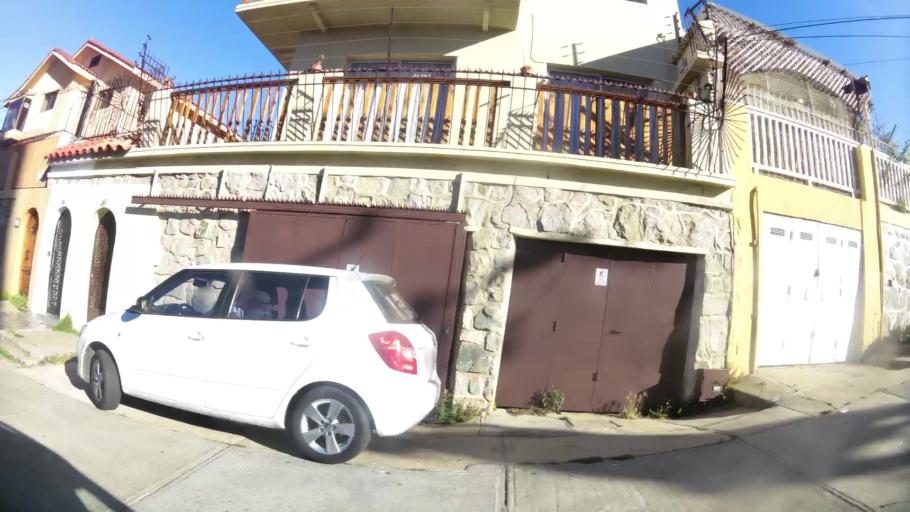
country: CL
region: Valparaiso
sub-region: Provincia de Valparaiso
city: Vina del Mar
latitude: -33.0275
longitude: -71.5702
